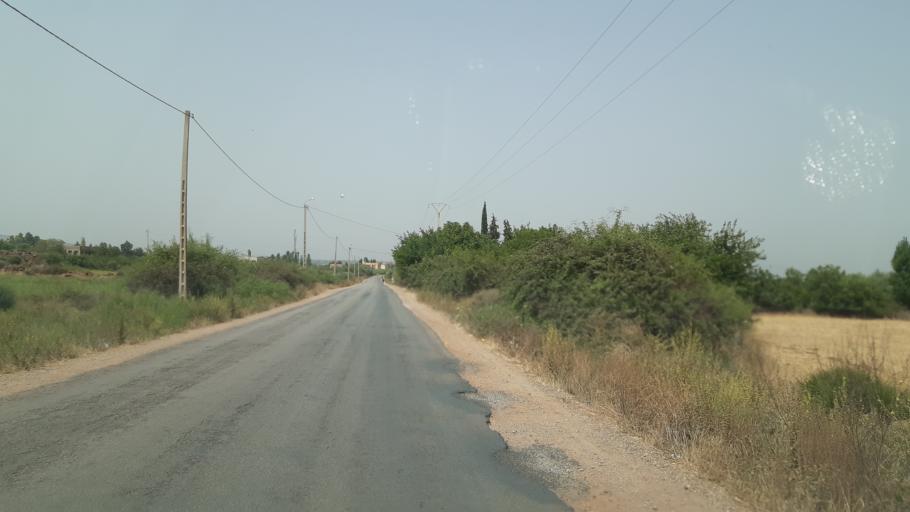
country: MA
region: Fes-Boulemane
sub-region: Fes
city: Oulad Tayeb
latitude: 33.8337
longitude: -5.1461
